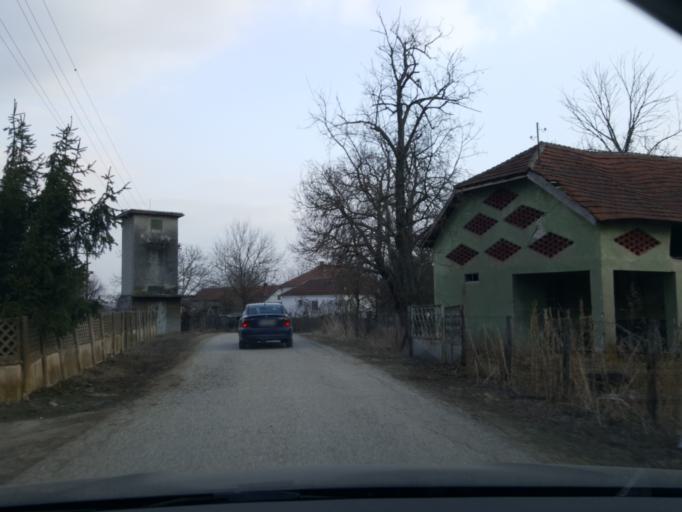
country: RS
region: Central Serbia
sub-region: Nisavski Okrug
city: Aleksinac
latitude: 43.5776
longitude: 21.6461
